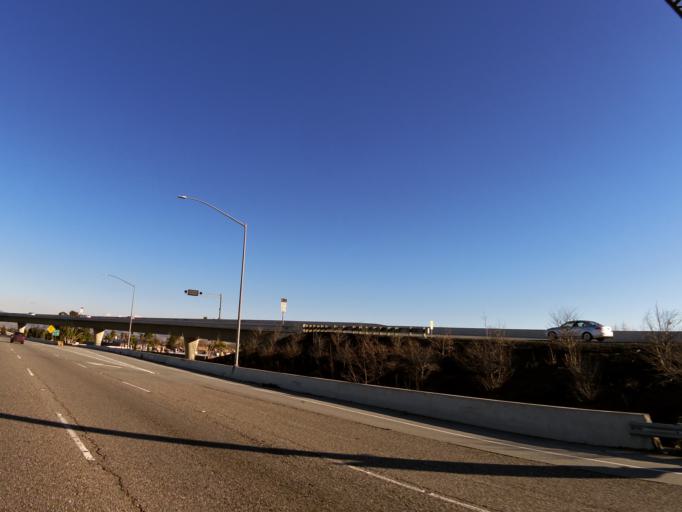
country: US
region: California
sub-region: Santa Clara County
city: Seven Trees
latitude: 37.2553
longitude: -121.8640
